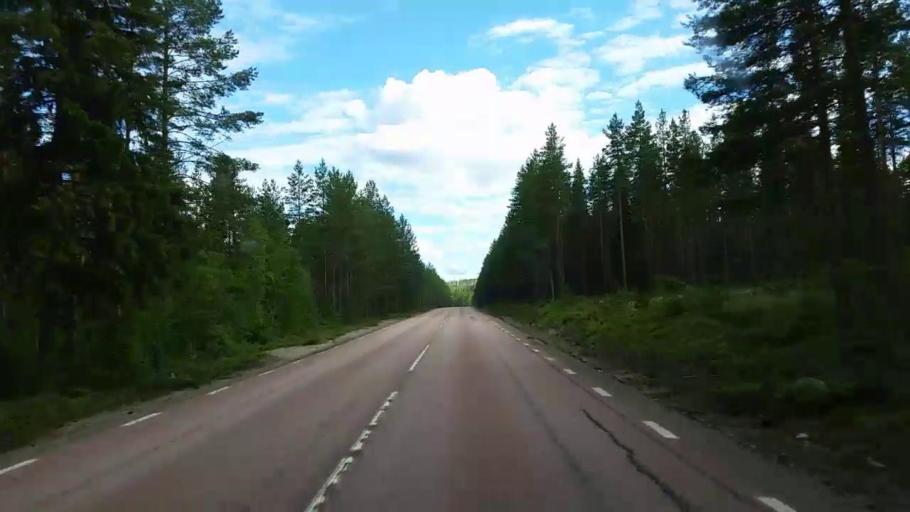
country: SE
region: Gaevleborg
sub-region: Ljusdals Kommun
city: Farila
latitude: 61.9829
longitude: 15.8567
